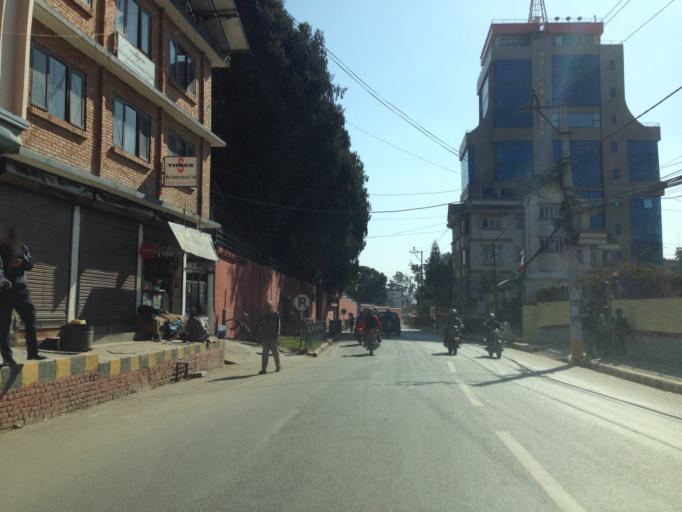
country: NP
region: Central Region
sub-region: Bagmati Zone
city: Kathmandu
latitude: 27.7288
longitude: 85.3310
